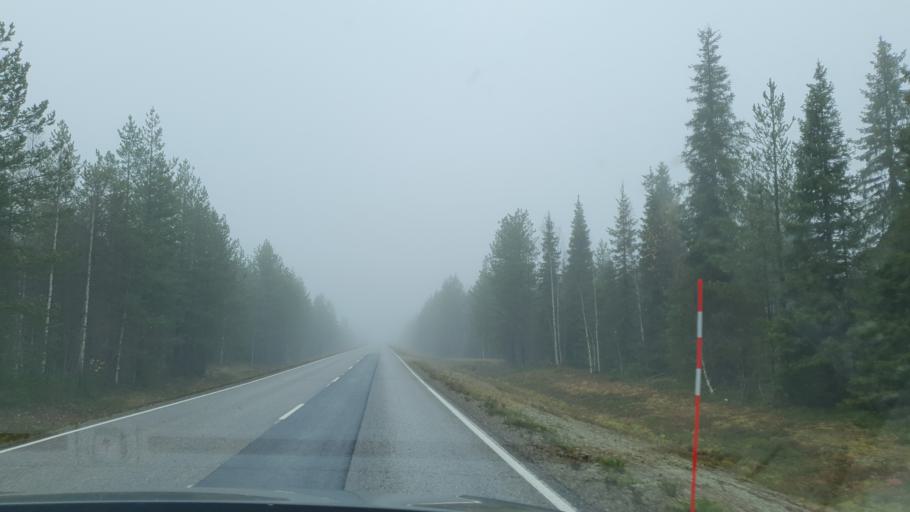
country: FI
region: Lapland
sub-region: Tunturi-Lappi
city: Kittilae
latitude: 67.2417
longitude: 24.9160
